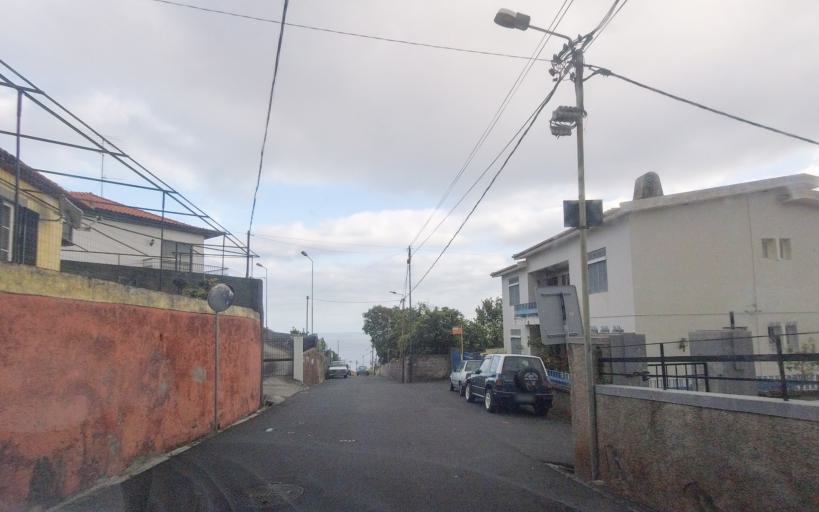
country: PT
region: Madeira
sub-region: Funchal
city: Nossa Senhora do Monte
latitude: 32.6519
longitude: -16.8884
